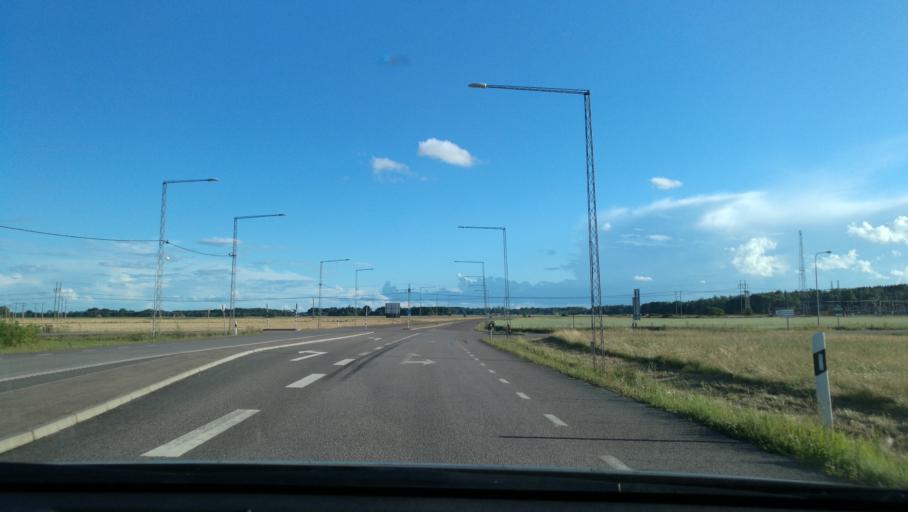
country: SE
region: Vaestmanland
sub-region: Kopings Kommun
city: Koping
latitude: 59.4976
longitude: 15.9933
